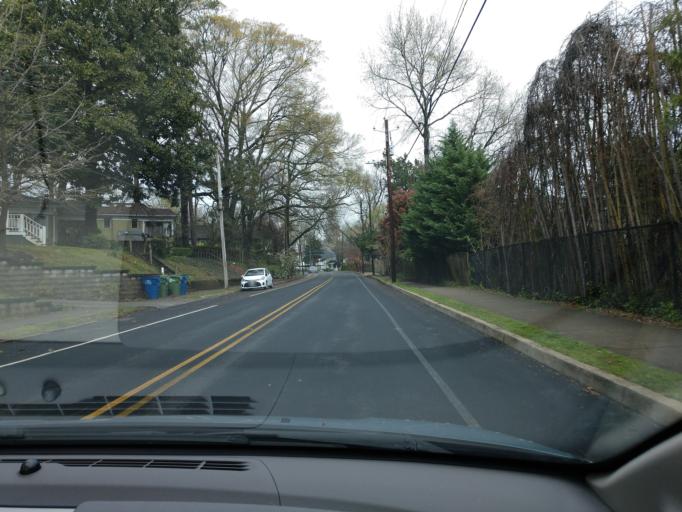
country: US
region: Georgia
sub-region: Fulton County
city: Atlanta
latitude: 33.7349
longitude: -84.3661
